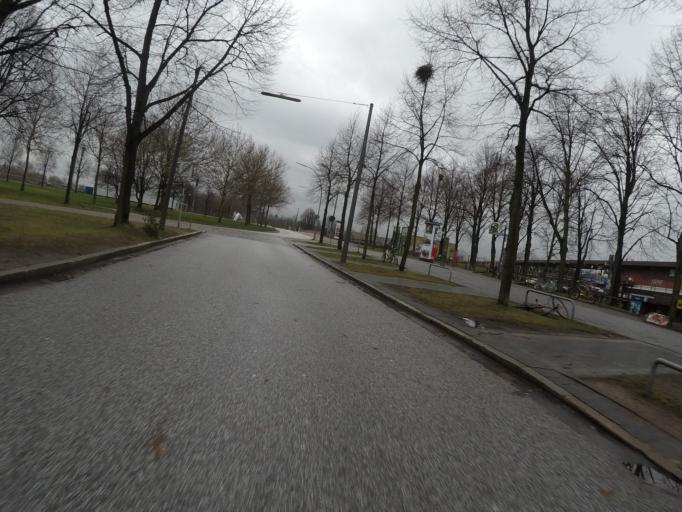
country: DE
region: Hamburg
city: Kleiner Grasbrook
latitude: 53.5231
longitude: 10.0151
